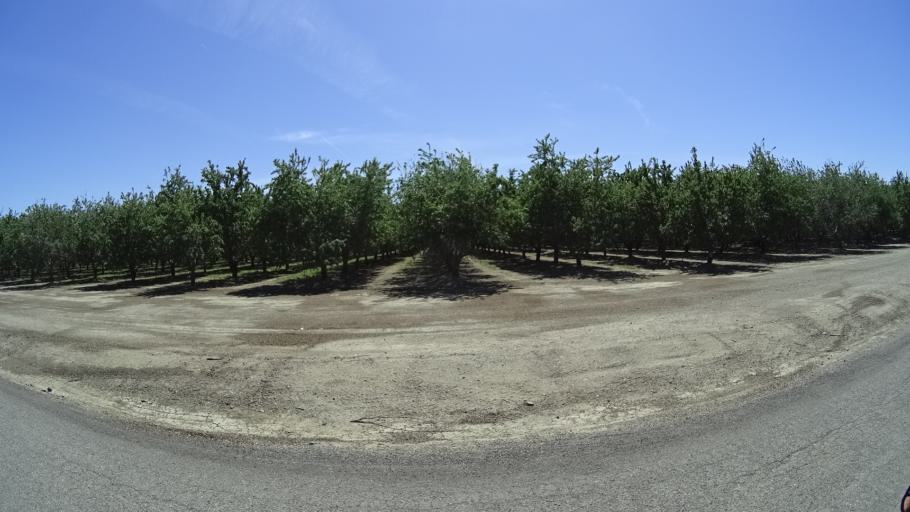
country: US
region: California
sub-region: Glenn County
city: Orland
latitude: 39.7323
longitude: -122.1379
